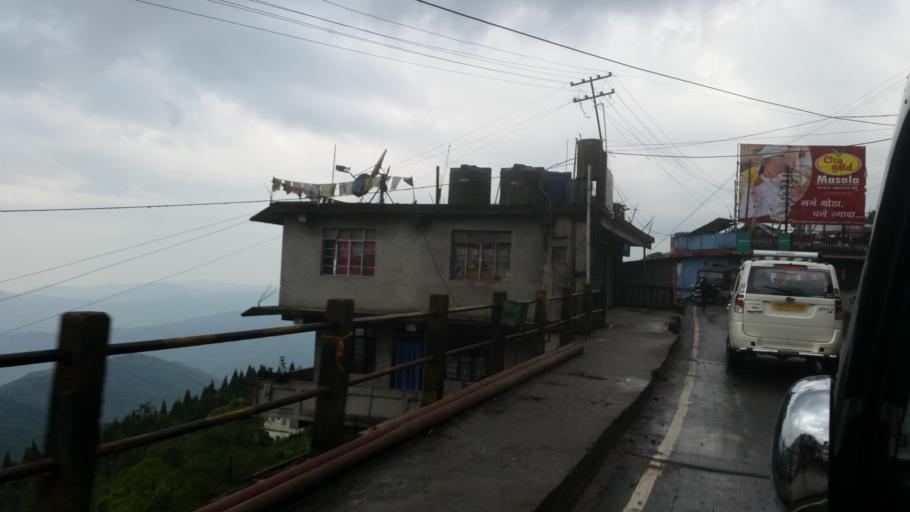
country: IN
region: West Bengal
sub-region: Darjiling
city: Darjiling
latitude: 27.0082
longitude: 88.2557
